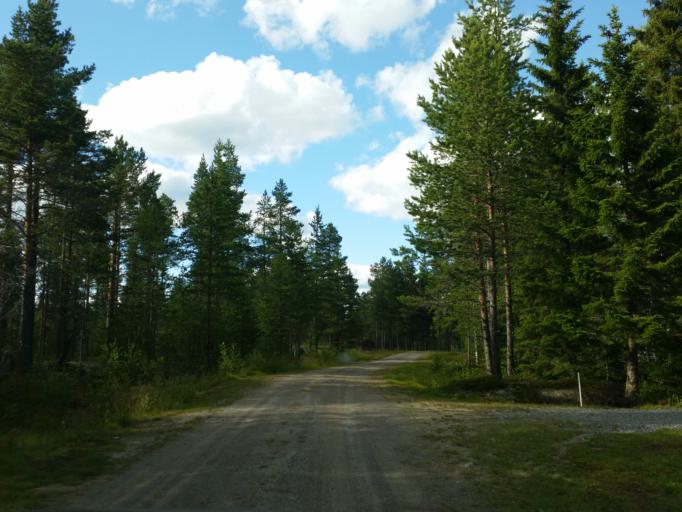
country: SE
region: Vaesterbotten
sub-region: Robertsfors Kommun
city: Robertsfors
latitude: 64.1305
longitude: 20.9489
